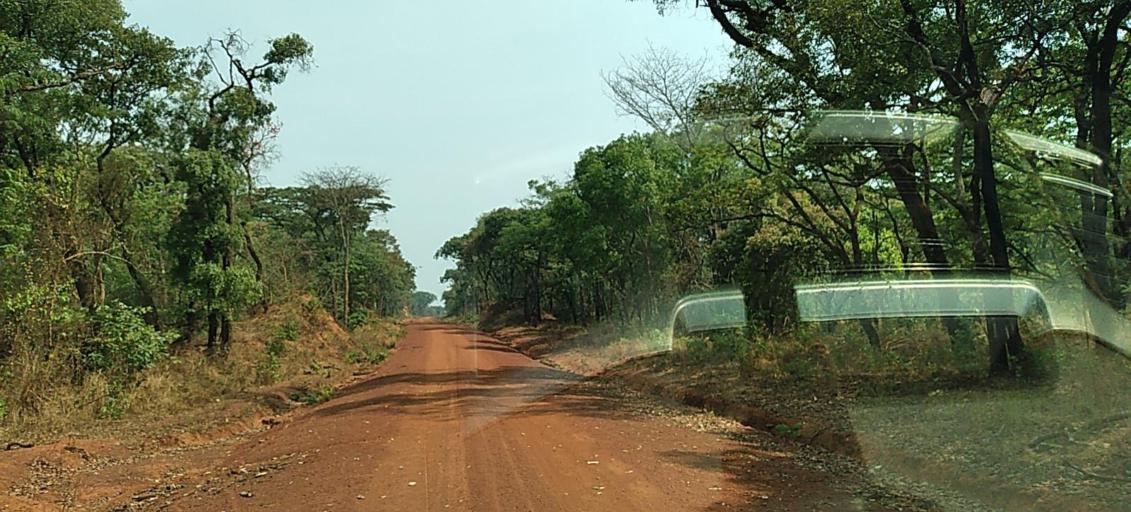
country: ZM
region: North-Western
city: Kansanshi
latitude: -12.0156
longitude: 26.8477
